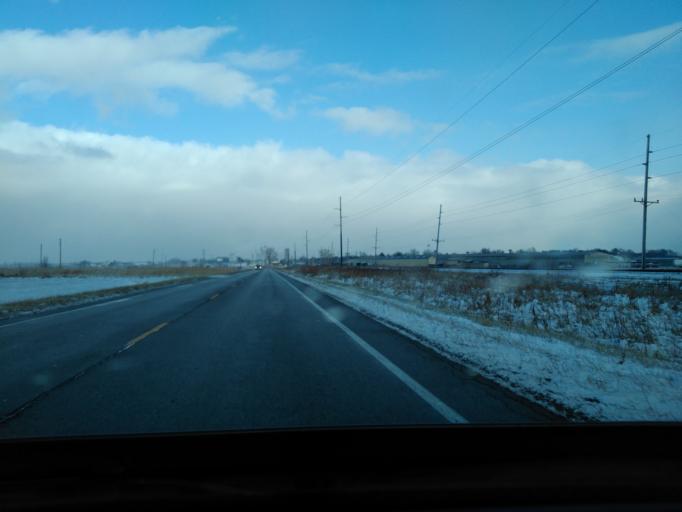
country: US
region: Illinois
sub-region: Madison County
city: Highland
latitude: 38.7377
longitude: -89.7027
